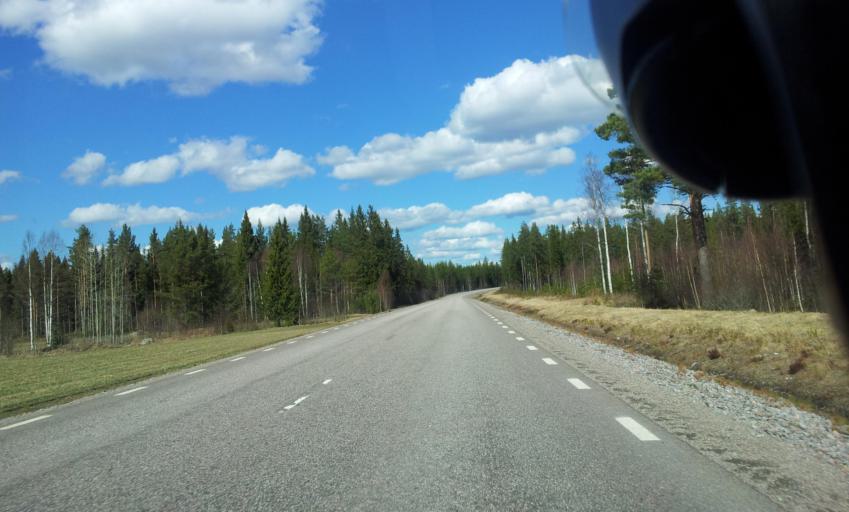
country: SE
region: Gaevleborg
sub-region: Ovanakers Kommun
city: Edsbyn
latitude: 61.2737
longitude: 15.8944
